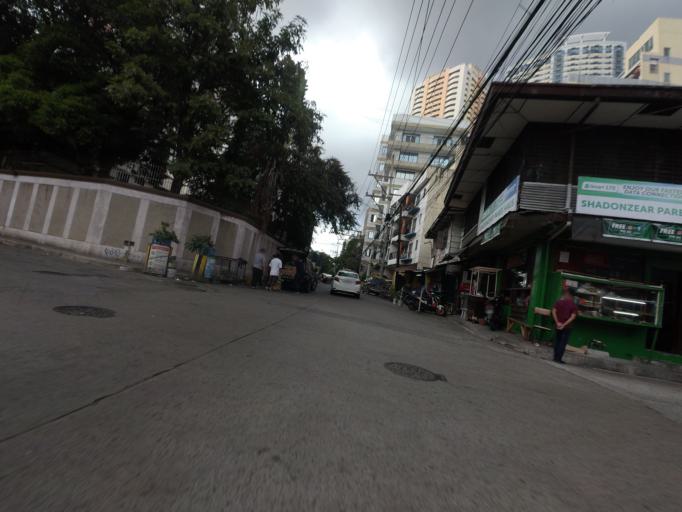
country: PH
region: Metro Manila
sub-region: City of Manila
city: Port Area
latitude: 14.5600
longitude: 120.9946
